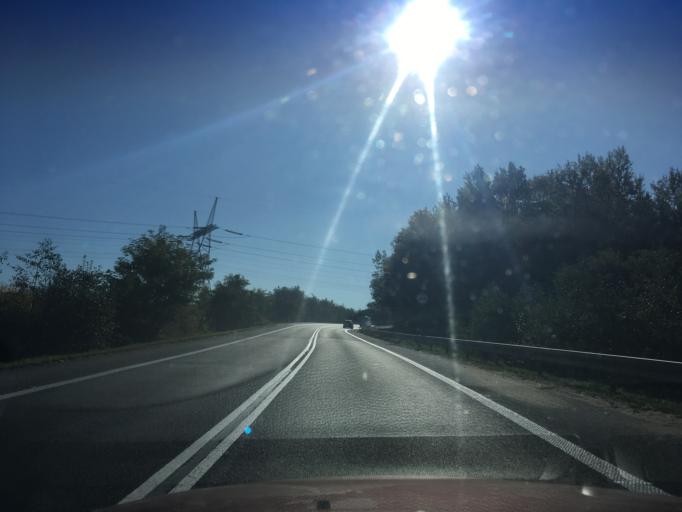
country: DE
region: Saxony
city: Ostritz
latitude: 50.9913
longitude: 14.9433
